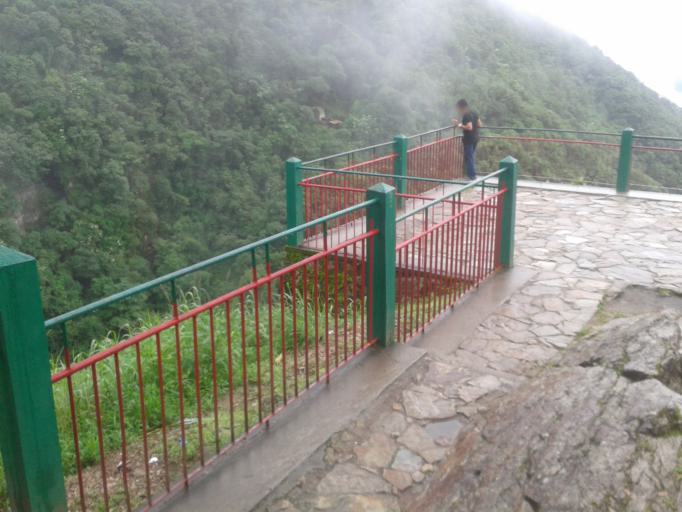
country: IN
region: Meghalaya
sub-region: East Khasi Hills
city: Cherrapunji
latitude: 25.4211
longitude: 91.7916
